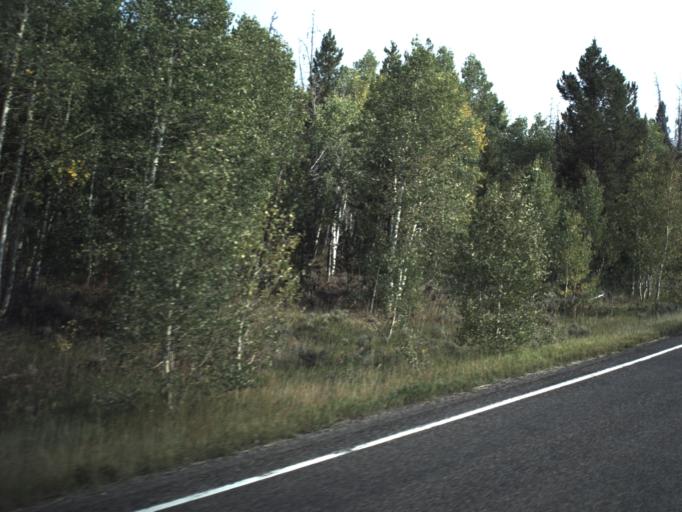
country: US
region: Wyoming
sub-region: Uinta County
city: Evanston
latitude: 40.8903
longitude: -110.8315
